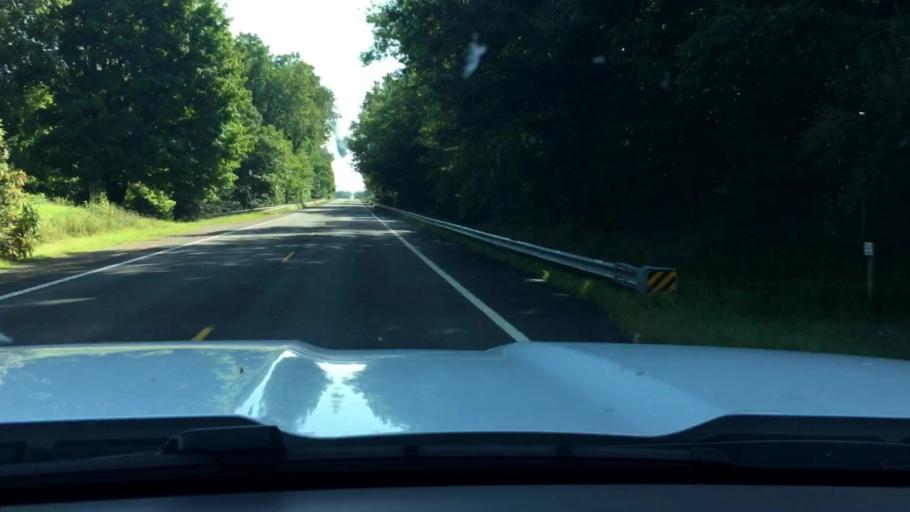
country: US
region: Michigan
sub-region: Montcalm County
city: Edmore
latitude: 43.4082
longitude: -84.8506
